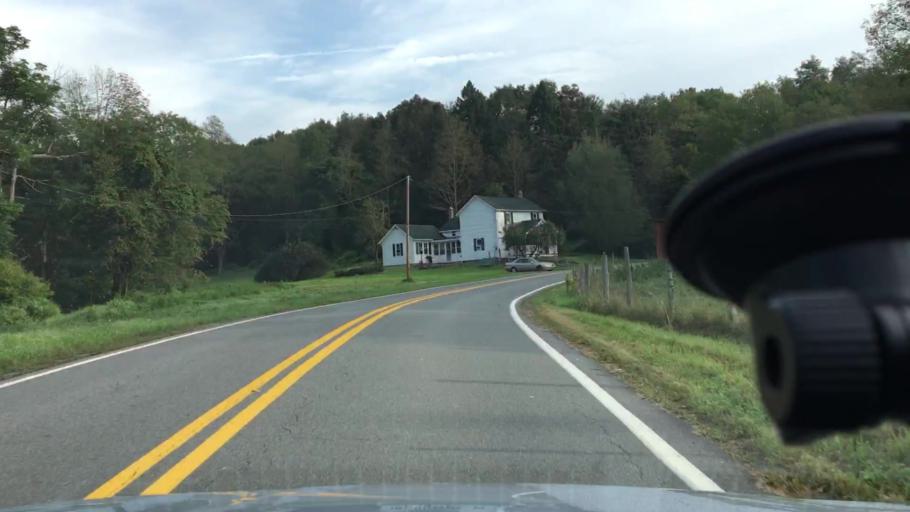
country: US
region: Pennsylvania
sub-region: Monroe County
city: Parkside
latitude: 41.1288
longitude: -75.2643
